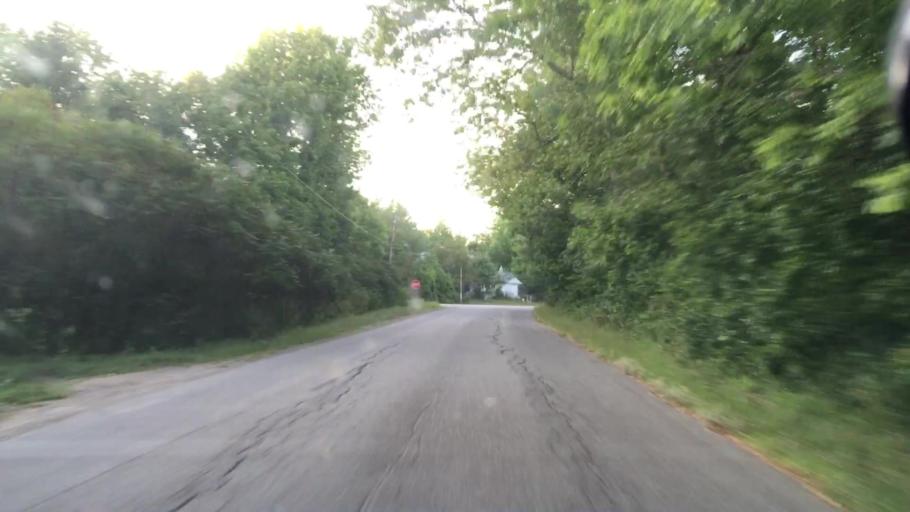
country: US
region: Maine
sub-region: Waldo County
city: Frankfort
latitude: 44.6711
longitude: -68.9262
